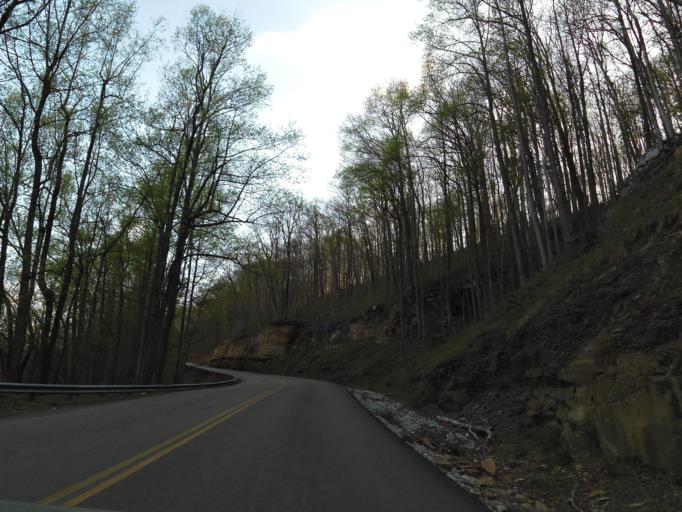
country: US
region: Kentucky
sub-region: Bell County
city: Middlesboro
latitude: 36.6360
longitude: -83.8522
